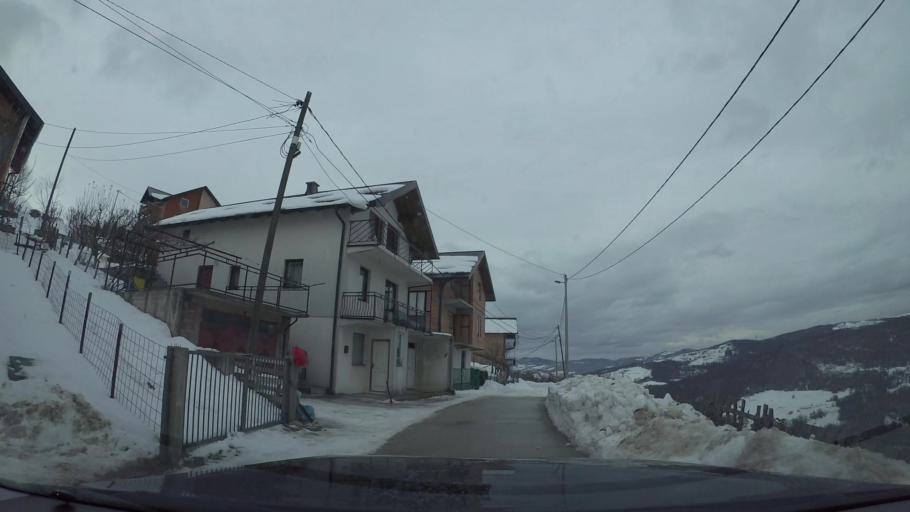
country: BA
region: Federation of Bosnia and Herzegovina
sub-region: Kanton Sarajevo
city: Sarajevo
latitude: 43.8640
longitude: 18.3543
